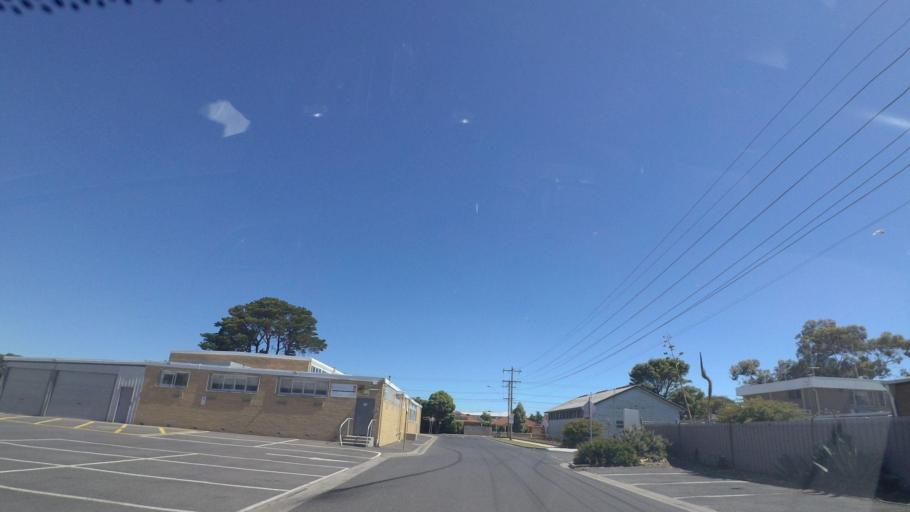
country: AU
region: Victoria
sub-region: Hobsons Bay
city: Altona
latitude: -37.8633
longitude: 144.8268
